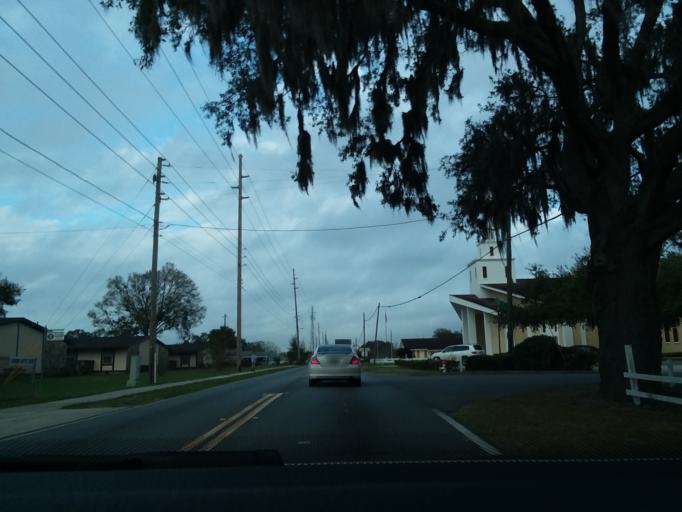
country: US
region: Florida
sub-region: Polk County
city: Haines City
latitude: 28.1068
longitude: -81.6128
